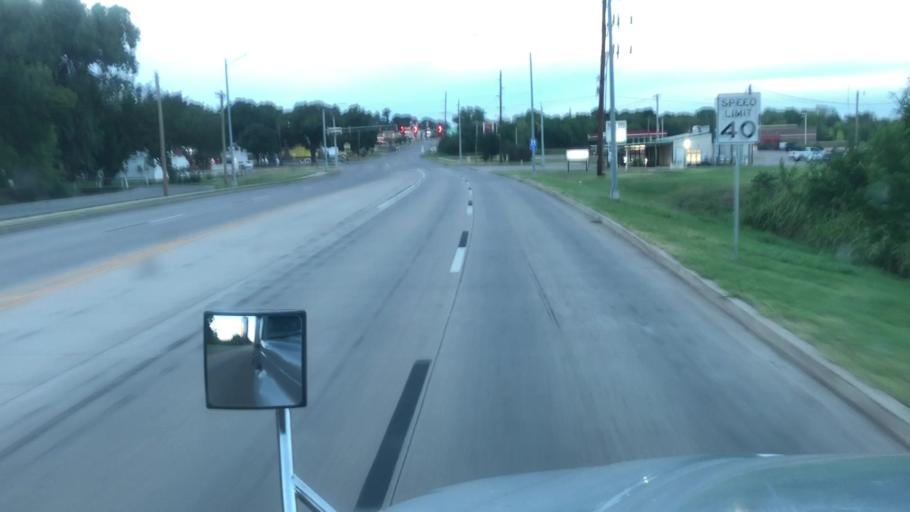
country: US
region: Oklahoma
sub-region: Kay County
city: Ponca City
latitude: 36.6939
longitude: -97.0669
